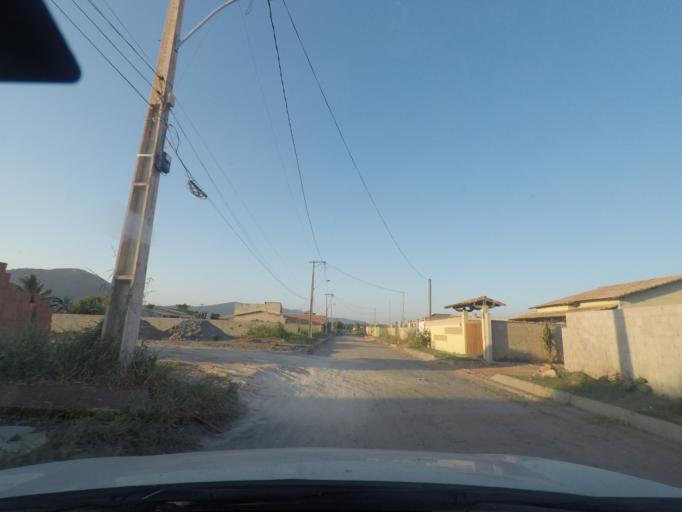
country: BR
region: Rio de Janeiro
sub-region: Marica
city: Marica
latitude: -22.9607
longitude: -42.9415
